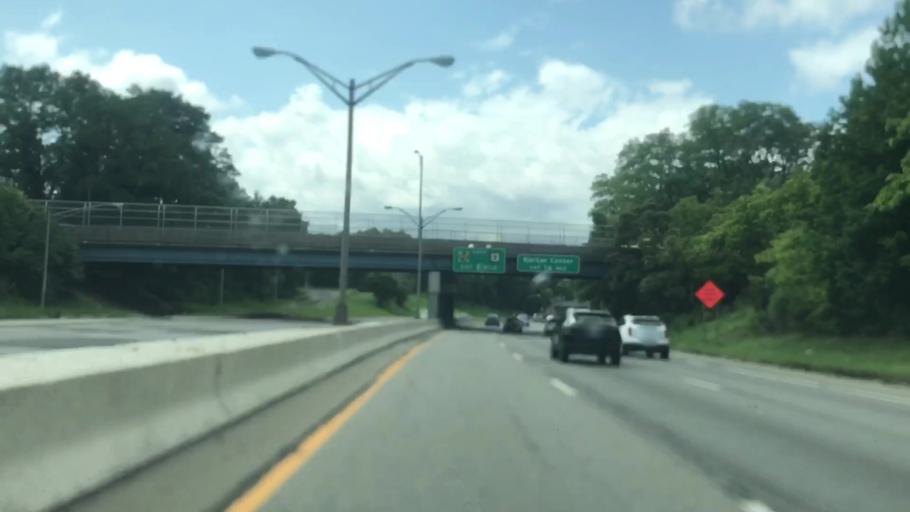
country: US
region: New Jersey
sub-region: Middlesex County
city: Fords
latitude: 40.5235
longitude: -74.2903
